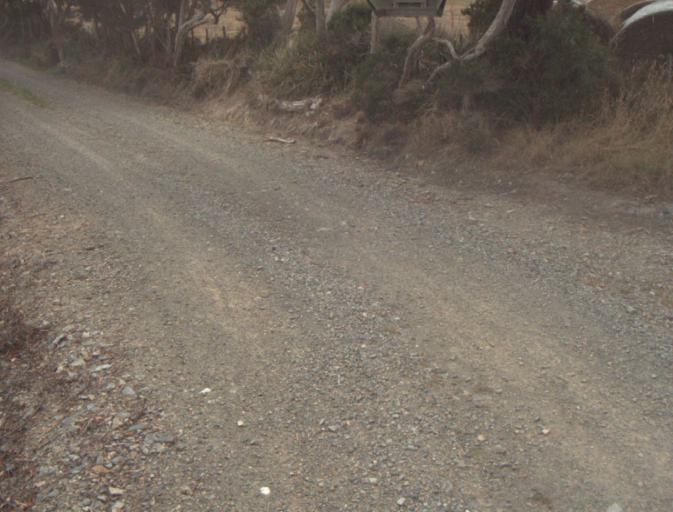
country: AU
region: Tasmania
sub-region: Launceston
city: Mayfield
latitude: -41.2429
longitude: 147.1647
